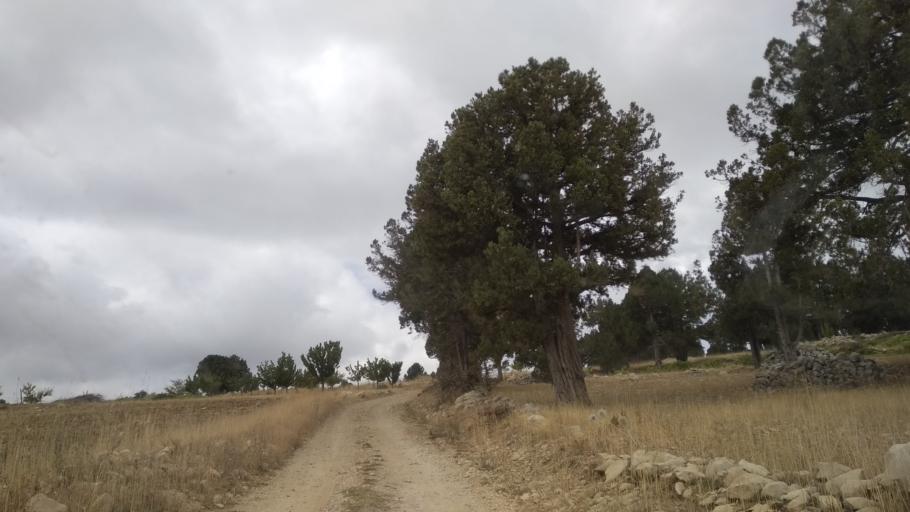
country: TR
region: Mersin
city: Sarikavak
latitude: 36.5654
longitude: 33.7673
